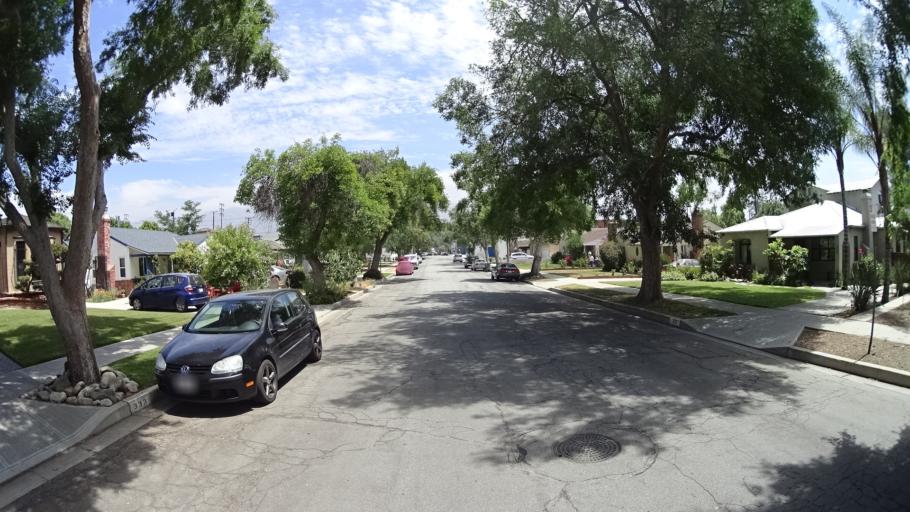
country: US
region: California
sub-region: Los Angeles County
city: Burbank
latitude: 34.1645
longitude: -118.3073
